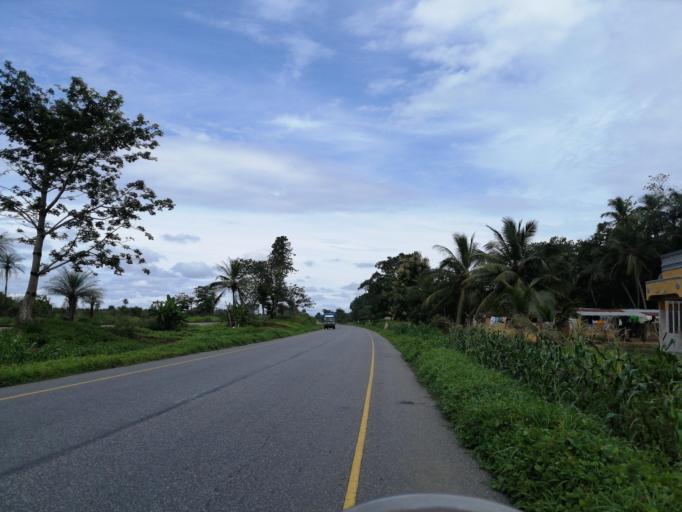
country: SL
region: Northern Province
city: Port Loko
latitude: 8.7421
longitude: -12.9386
